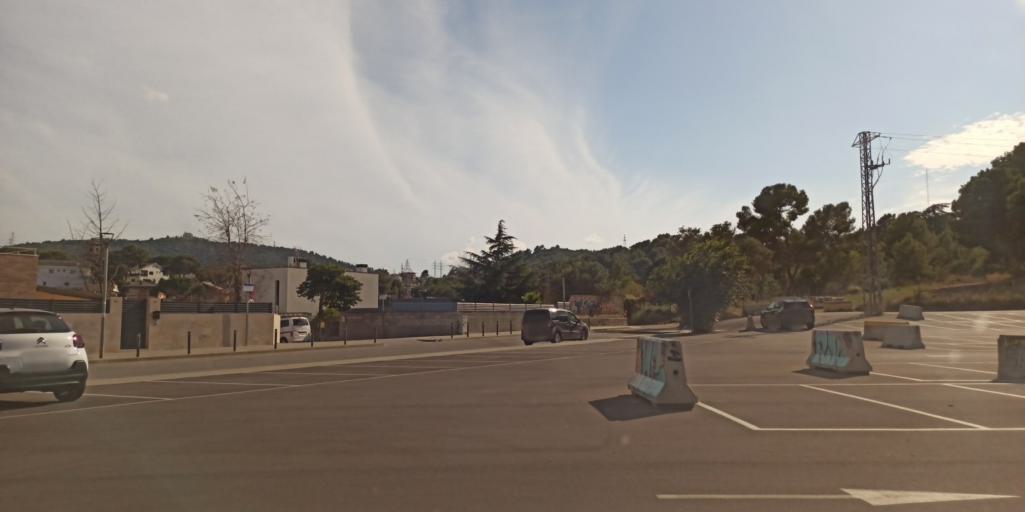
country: ES
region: Catalonia
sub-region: Provincia de Barcelona
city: Santa Coloma de Cervello
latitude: 41.3558
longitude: 2.0225
